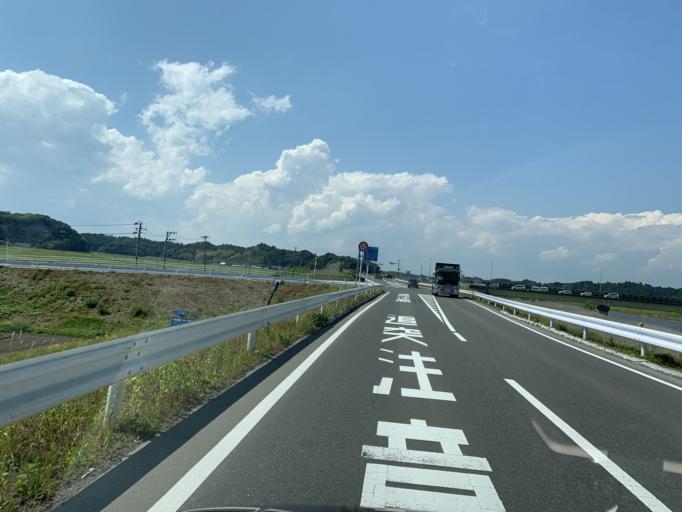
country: JP
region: Miyagi
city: Yamoto
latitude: 38.3940
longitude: 141.1564
